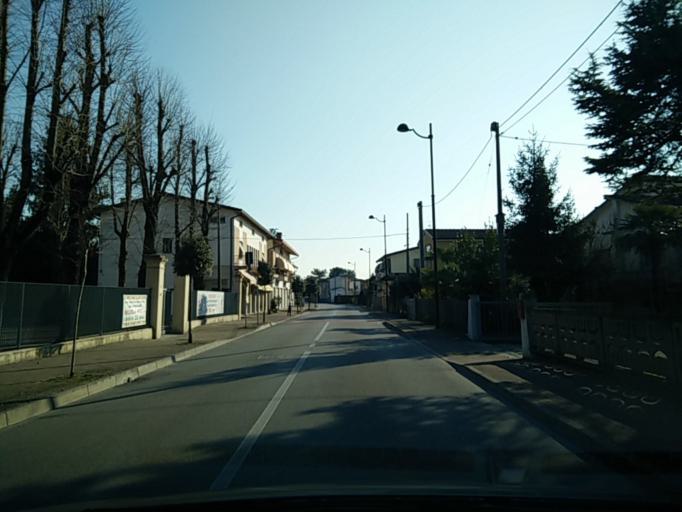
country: IT
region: Veneto
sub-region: Provincia di Venezia
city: Torre di Mosto
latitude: 45.6958
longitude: 12.7085
